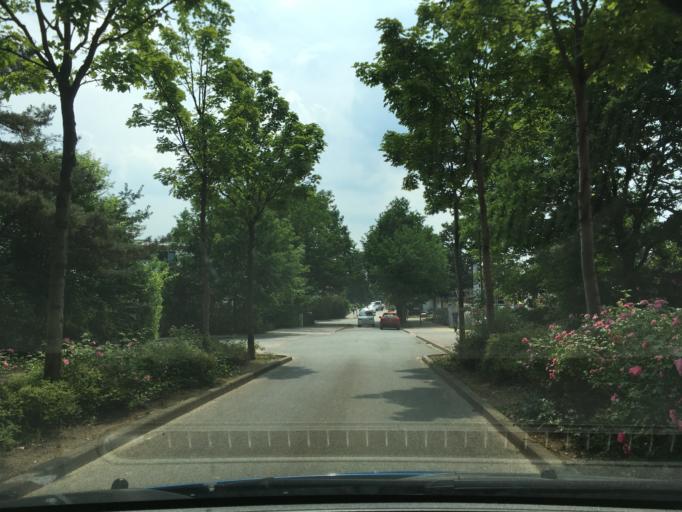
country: DE
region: Lower Saxony
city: Buchholz in der Nordheide
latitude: 53.3366
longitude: 9.8872
